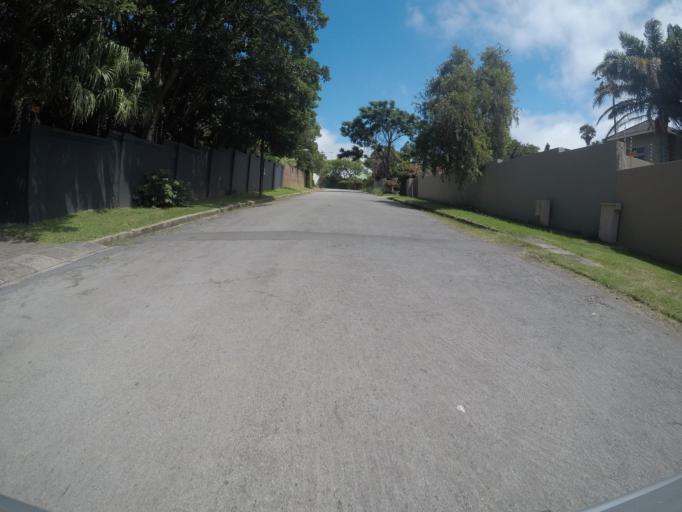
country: ZA
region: Eastern Cape
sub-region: Buffalo City Metropolitan Municipality
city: East London
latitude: -32.9739
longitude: 27.9050
